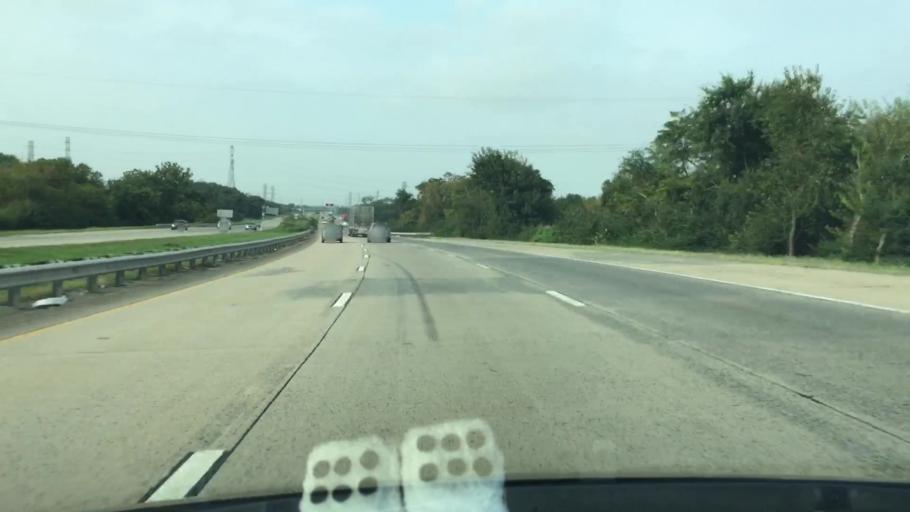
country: US
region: Delaware
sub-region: New Castle County
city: Edgemoor
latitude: 39.7469
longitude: -75.5102
